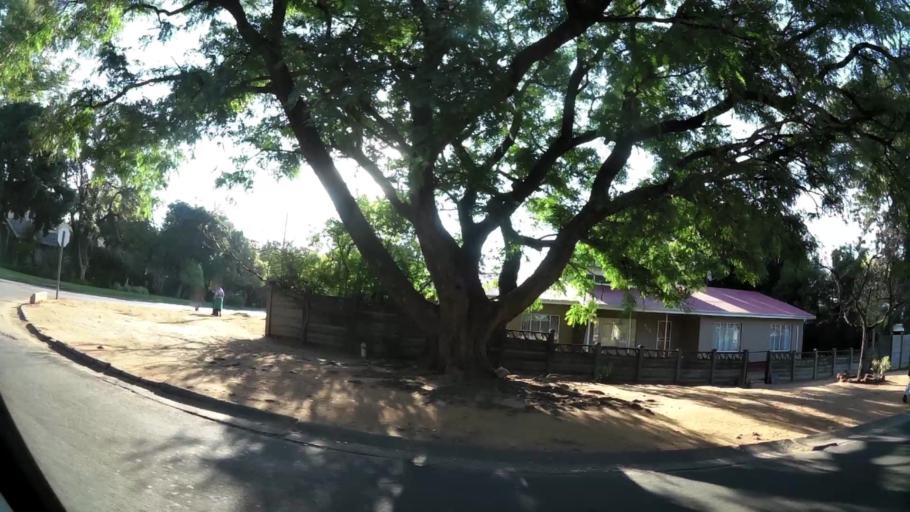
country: ZA
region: North-West
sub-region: Bojanala Platinum District Municipality
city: Rustenburg
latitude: -25.6818
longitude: 27.2282
